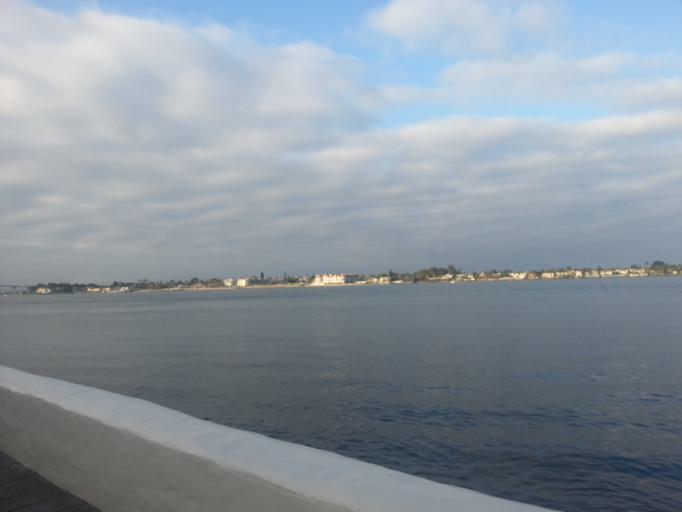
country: US
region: California
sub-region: San Diego County
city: San Diego
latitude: 32.7090
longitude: -117.1719
